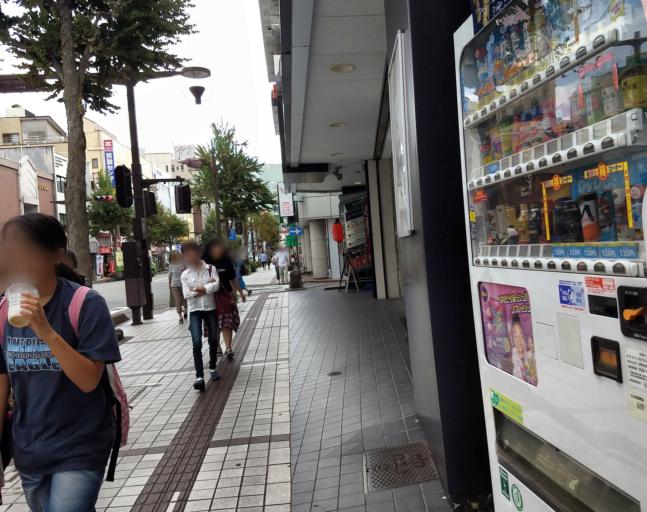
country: JP
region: Nagano
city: Nagano-shi
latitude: 36.6460
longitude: 138.1868
